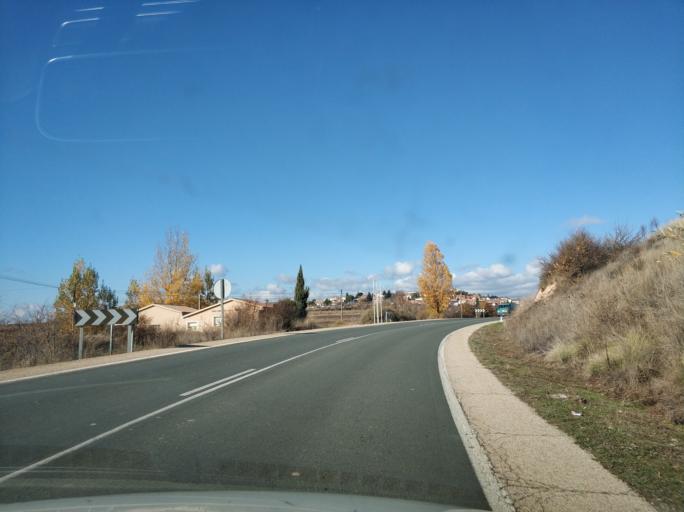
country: ES
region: Castille and Leon
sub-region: Provincia de Soria
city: Almazan
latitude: 41.4749
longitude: -2.5299
